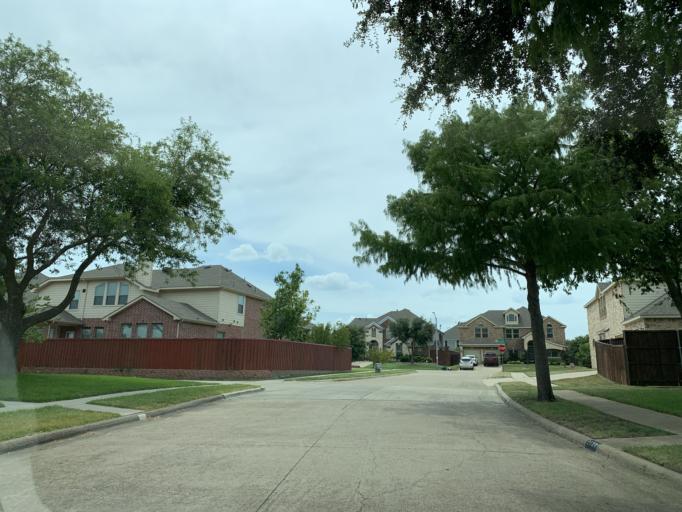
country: US
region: Texas
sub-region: Dallas County
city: Grand Prairie
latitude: 32.6563
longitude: -97.0348
